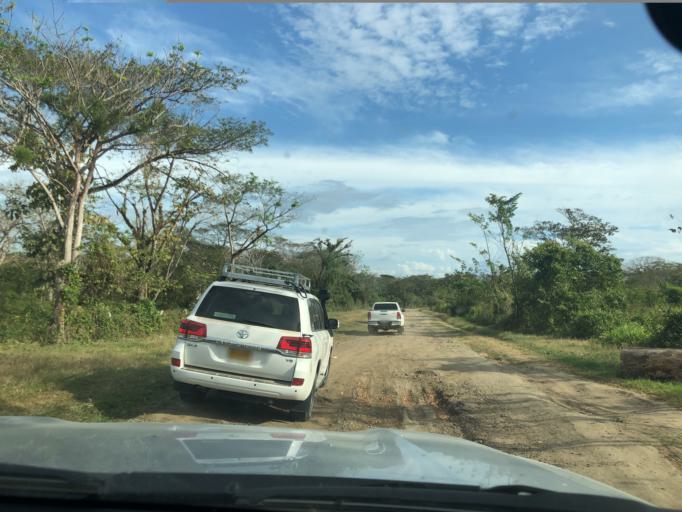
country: CR
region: Alajuela
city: San Jose
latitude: 11.1173
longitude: -85.2840
